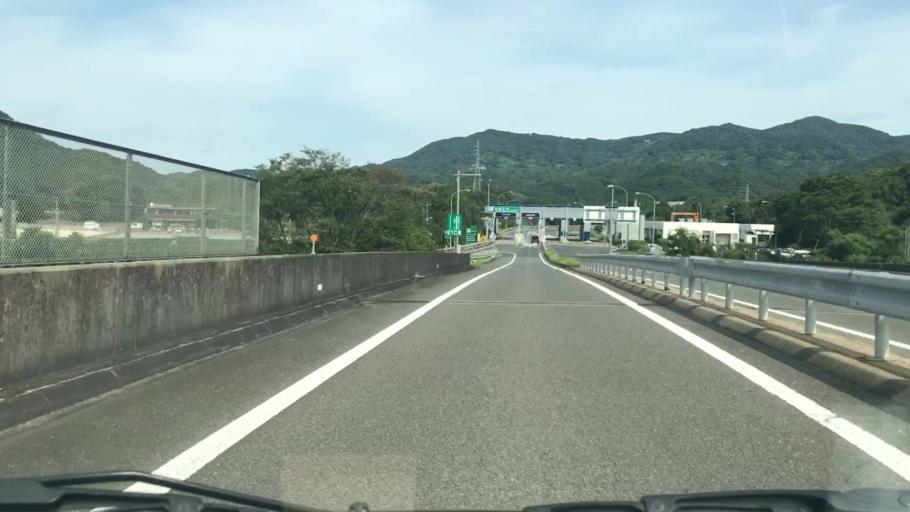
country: JP
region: Saga Prefecture
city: Takeocho-takeo
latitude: 33.2154
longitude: 130.0502
